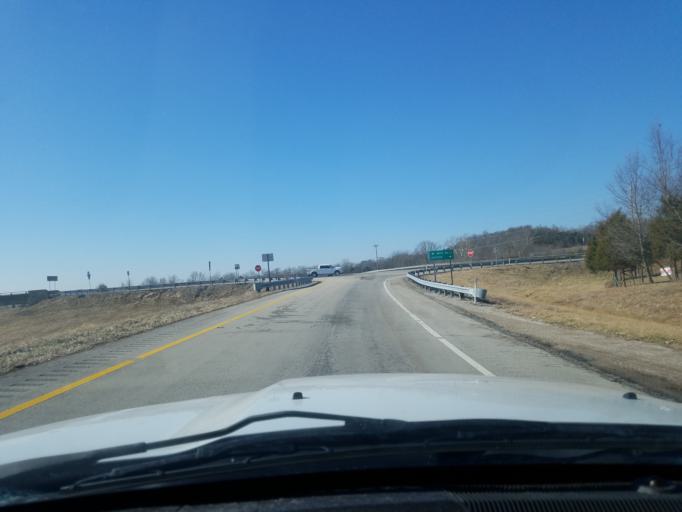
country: US
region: Kentucky
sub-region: Hardin County
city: Elizabethtown
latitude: 37.5724
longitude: -86.0365
